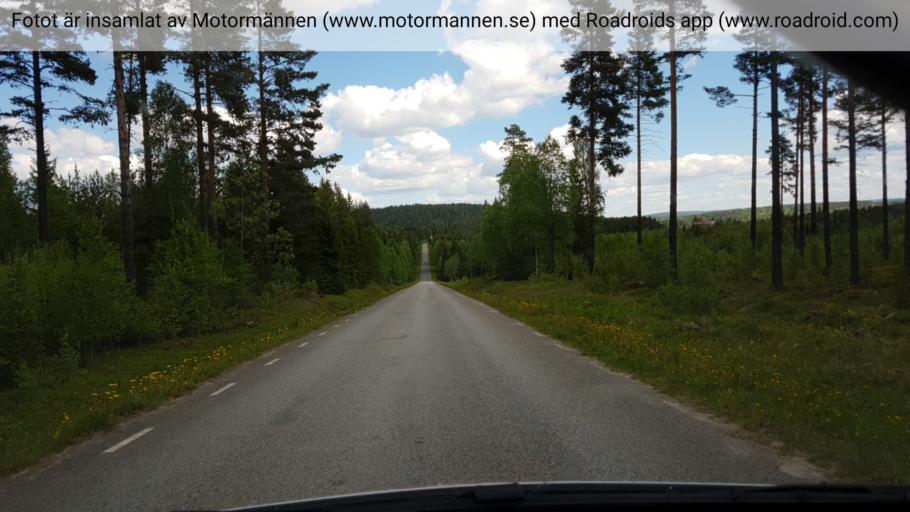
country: SE
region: Jaemtland
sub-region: OEstersunds Kommun
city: Brunflo
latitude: 62.9581
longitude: 15.1084
